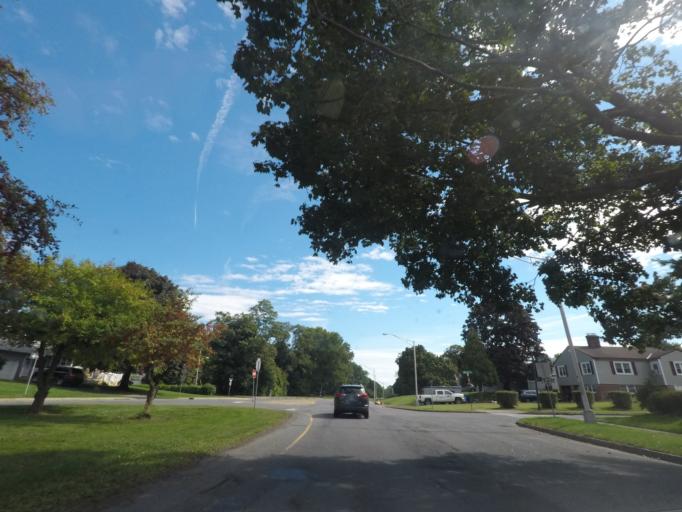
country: US
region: New York
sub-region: Albany County
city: West Albany
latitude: 42.6503
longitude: -73.7989
